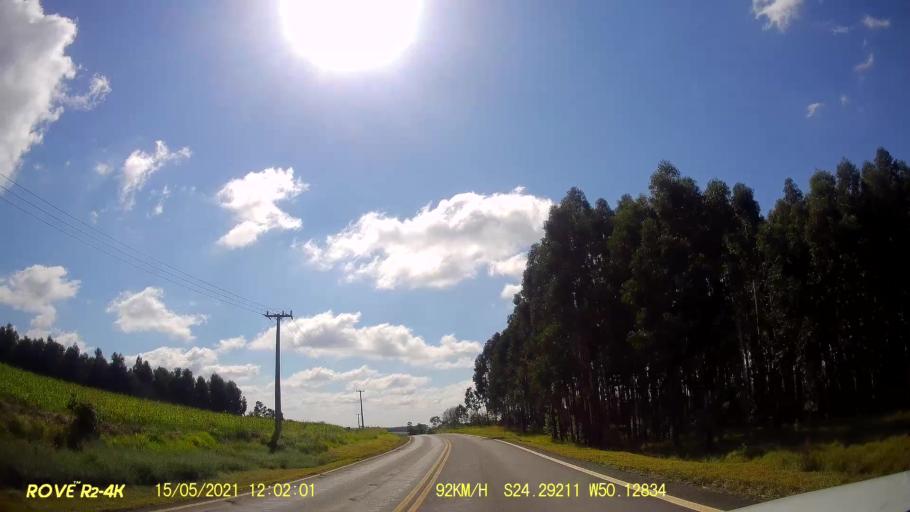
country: BR
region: Parana
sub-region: Pirai Do Sul
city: Pirai do Sul
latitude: -24.2920
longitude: -50.1285
